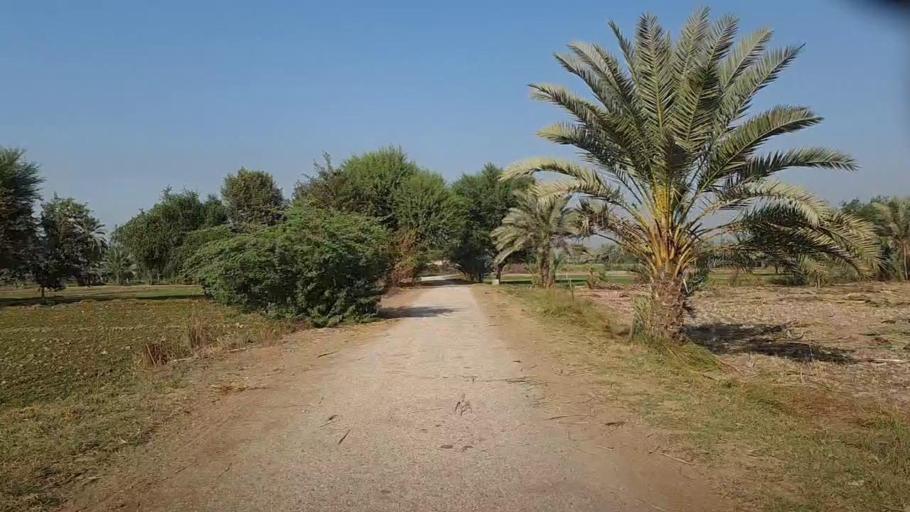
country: PK
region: Sindh
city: Ranipur
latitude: 27.2522
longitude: 68.5502
